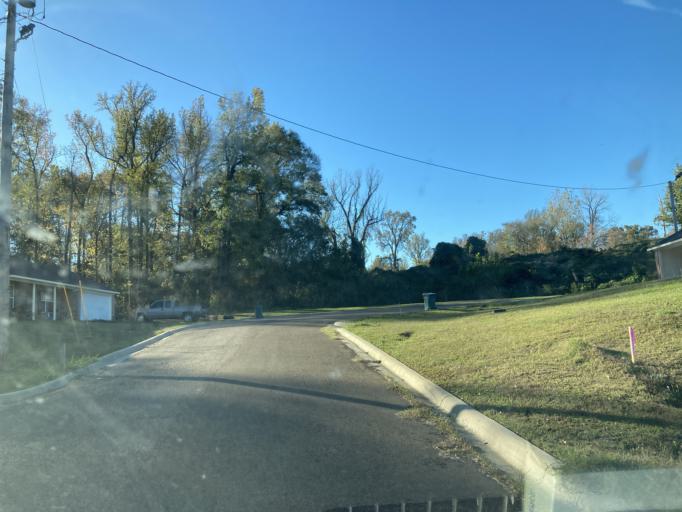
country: US
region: Mississippi
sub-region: Yazoo County
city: Yazoo City
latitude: 32.8480
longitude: -90.4032
